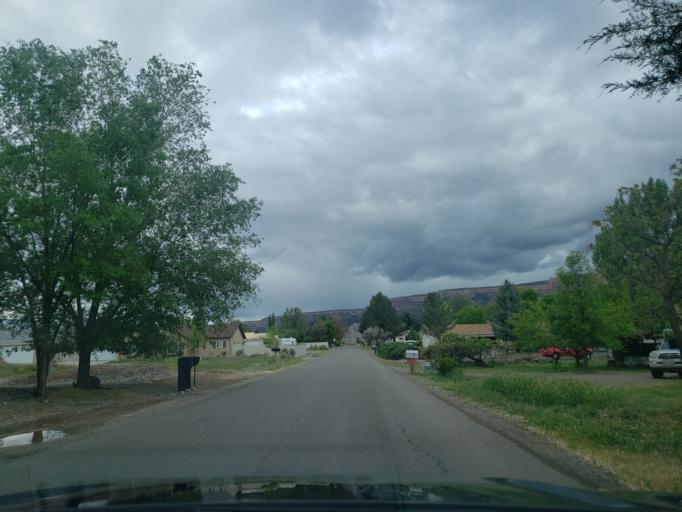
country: US
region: Colorado
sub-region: Mesa County
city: Redlands
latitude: 39.0947
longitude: -108.6625
